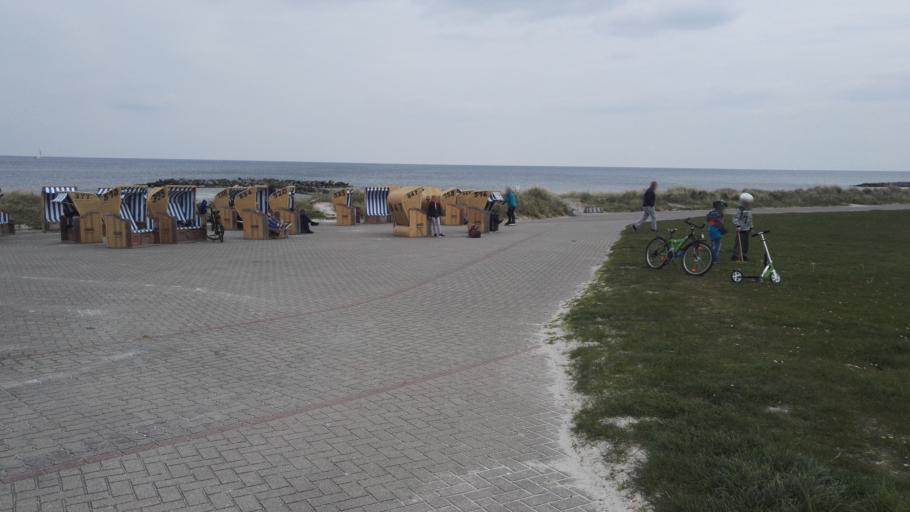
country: DE
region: Schleswig-Holstein
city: Krummbek
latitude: 54.4143
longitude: 10.4142
